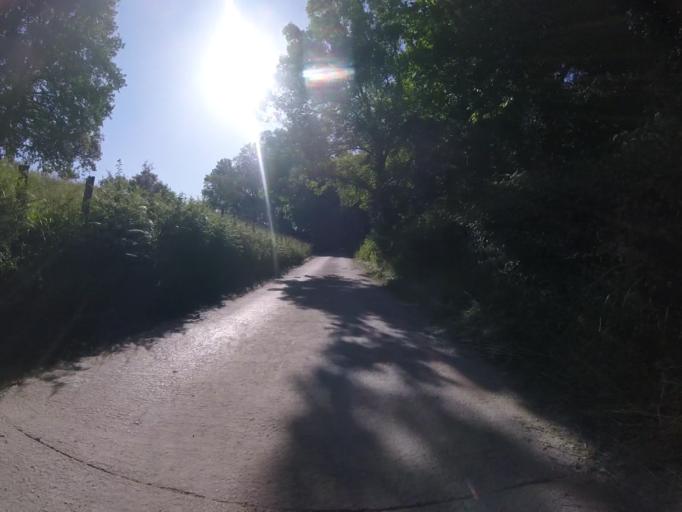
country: ES
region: Basque Country
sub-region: Provincia de Guipuzcoa
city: Astigarraga
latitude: 43.2944
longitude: -1.9312
